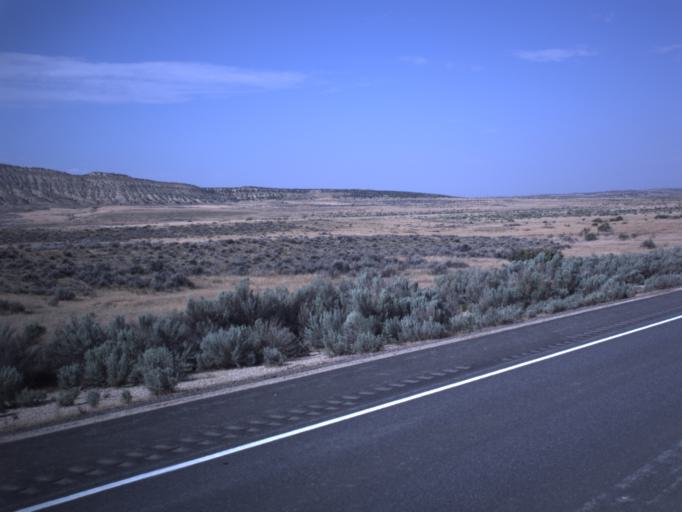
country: US
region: Colorado
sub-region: Rio Blanco County
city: Rangely
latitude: 40.2839
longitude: -109.1088
